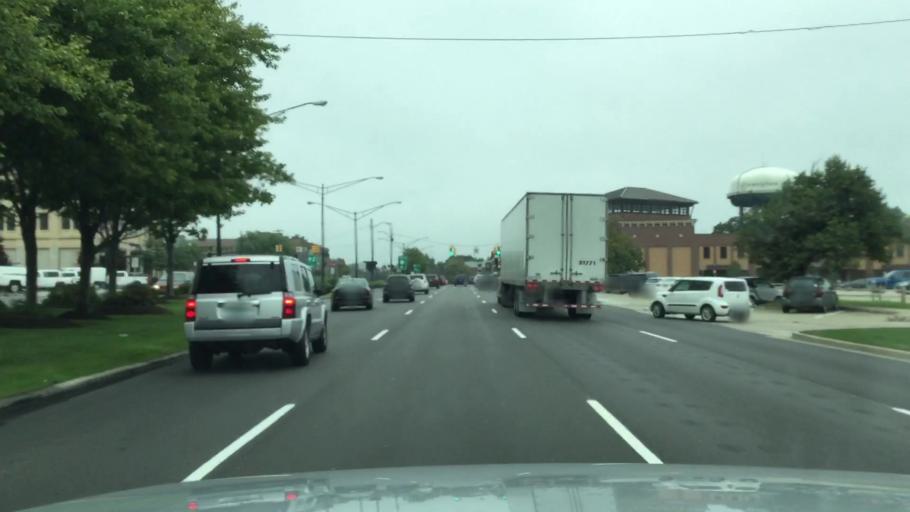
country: US
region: Michigan
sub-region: Oakland County
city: Birmingham
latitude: 42.5457
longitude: -83.2107
